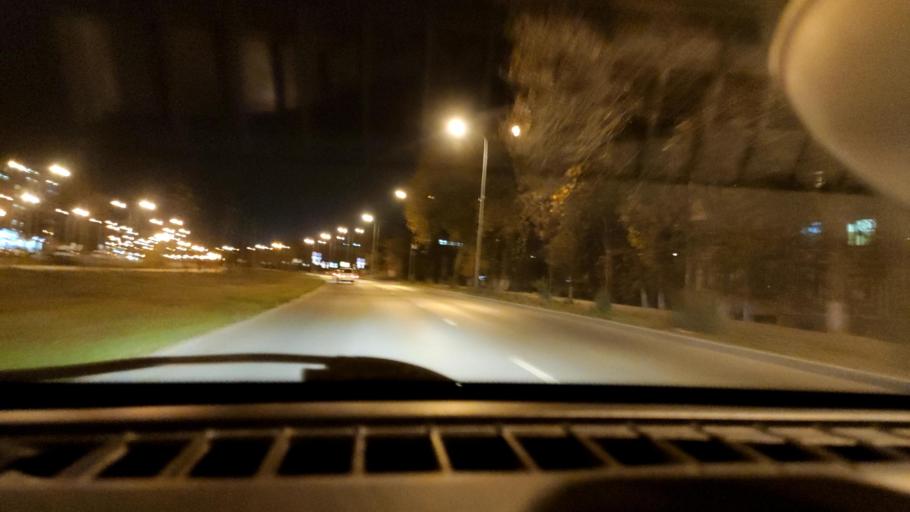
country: RU
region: Samara
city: Samara
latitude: 53.2539
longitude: 50.2473
